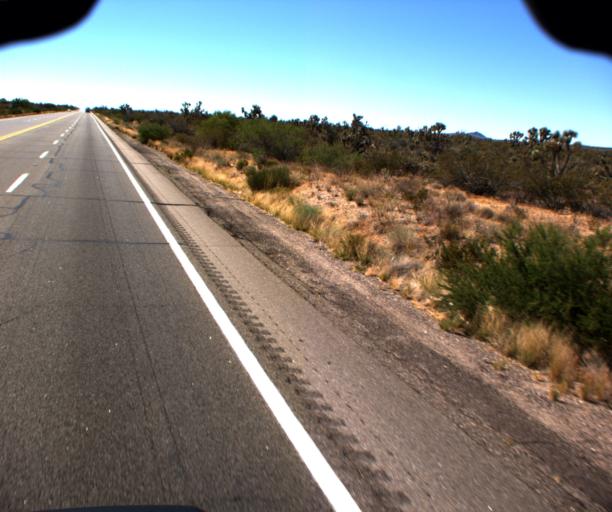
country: US
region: Arizona
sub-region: Yavapai County
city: Congress
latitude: 34.2879
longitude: -113.1084
